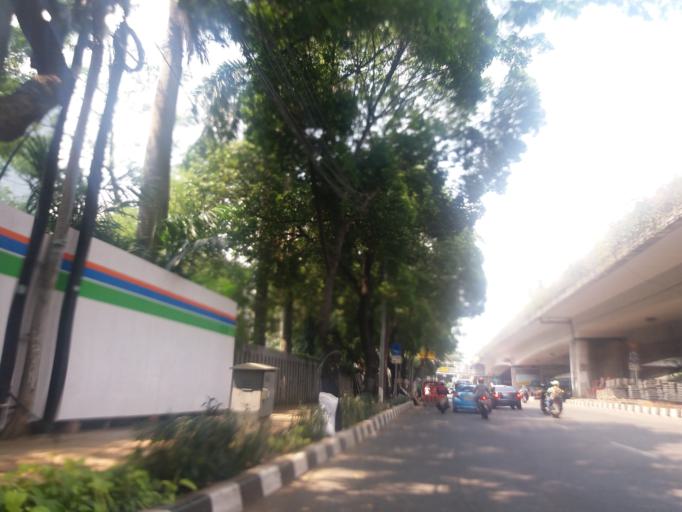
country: ID
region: Jakarta Raya
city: Jakarta
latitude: -6.2360
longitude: 106.8264
